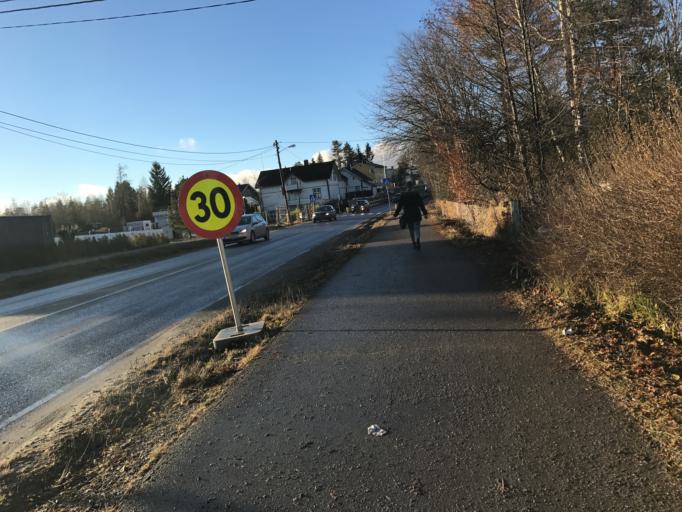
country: NO
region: Akershus
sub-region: Ullensaker
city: Jessheim
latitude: 60.1406
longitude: 11.1867
